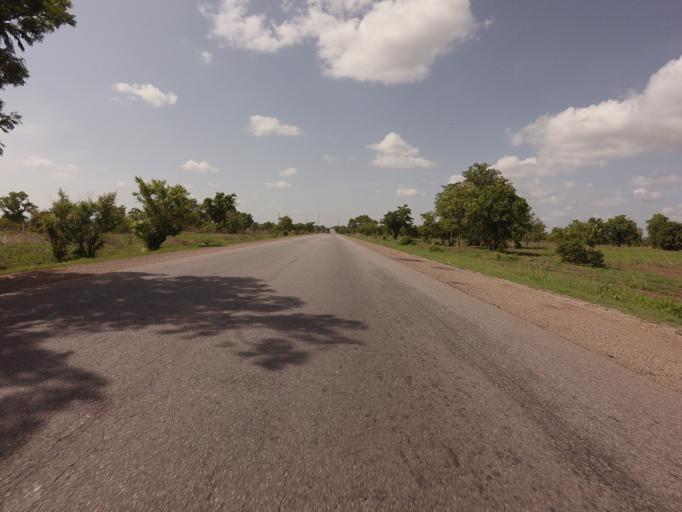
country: GH
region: Northern
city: Savelugu
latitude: 9.9690
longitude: -0.8294
